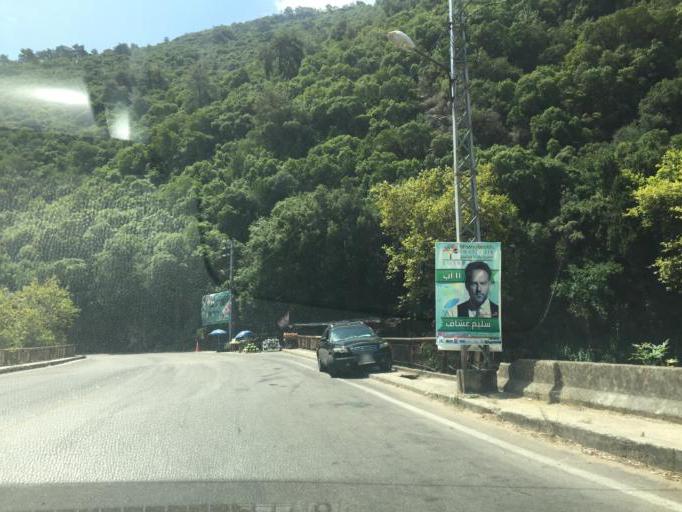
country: LB
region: Mont-Liban
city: Beit ed Dine
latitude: 33.7013
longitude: 35.4685
